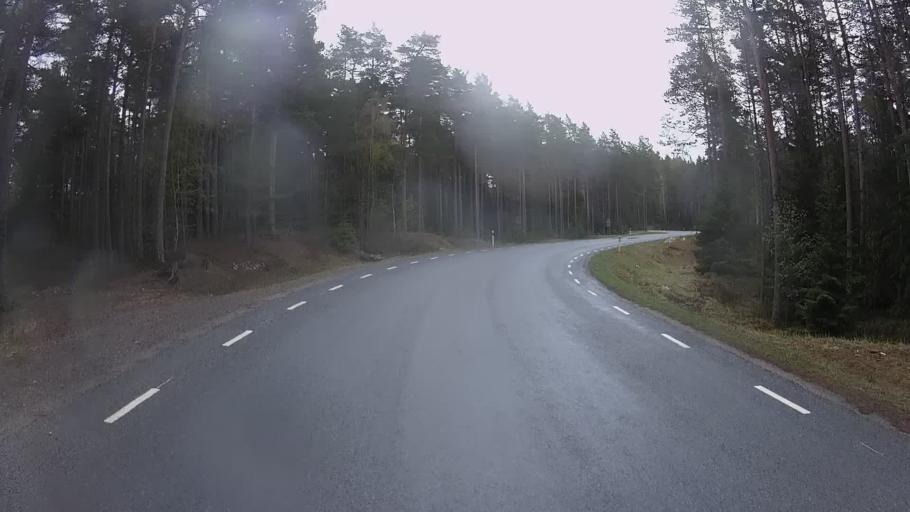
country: EE
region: Hiiumaa
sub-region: Kaerdla linn
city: Kardla
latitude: 58.9092
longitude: 22.3943
